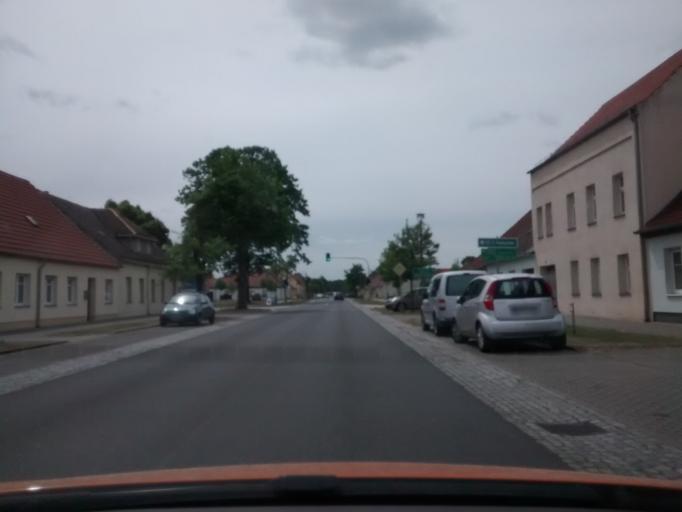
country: DE
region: Brandenburg
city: Juterbog
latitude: 52.0234
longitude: 13.1045
